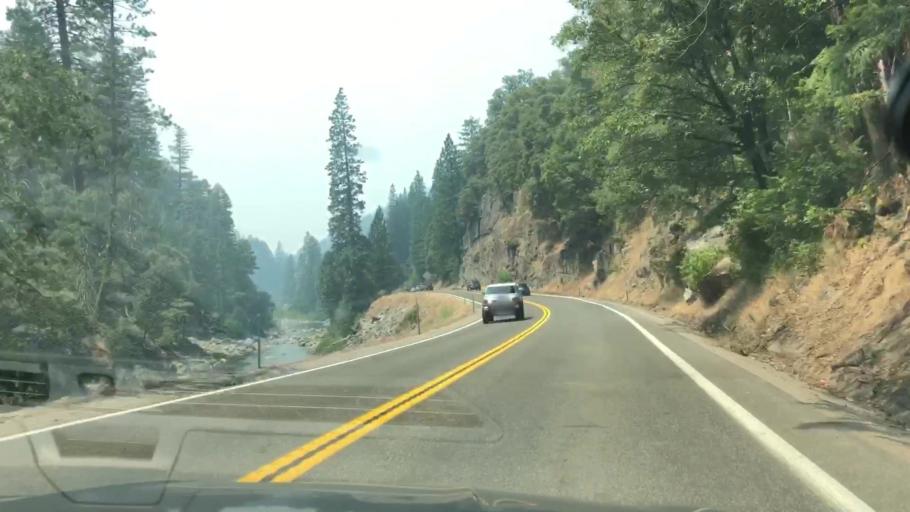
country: US
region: California
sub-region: El Dorado County
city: Pollock Pines
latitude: 38.7639
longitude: -120.3616
